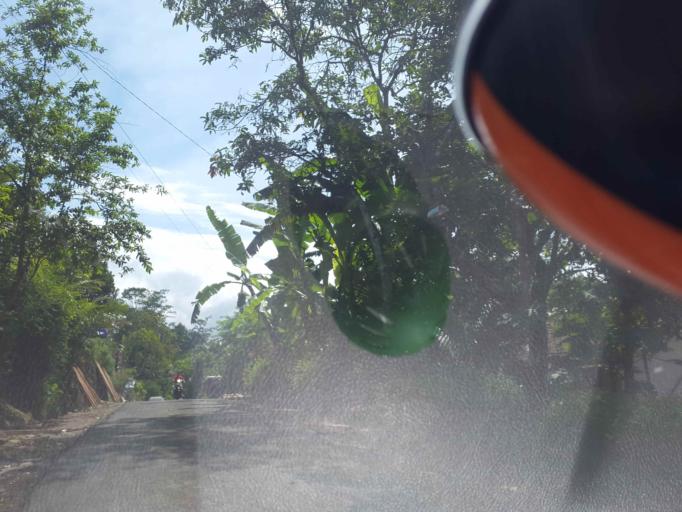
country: ID
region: Central Java
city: Wonosobo
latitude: -7.3542
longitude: 109.6937
